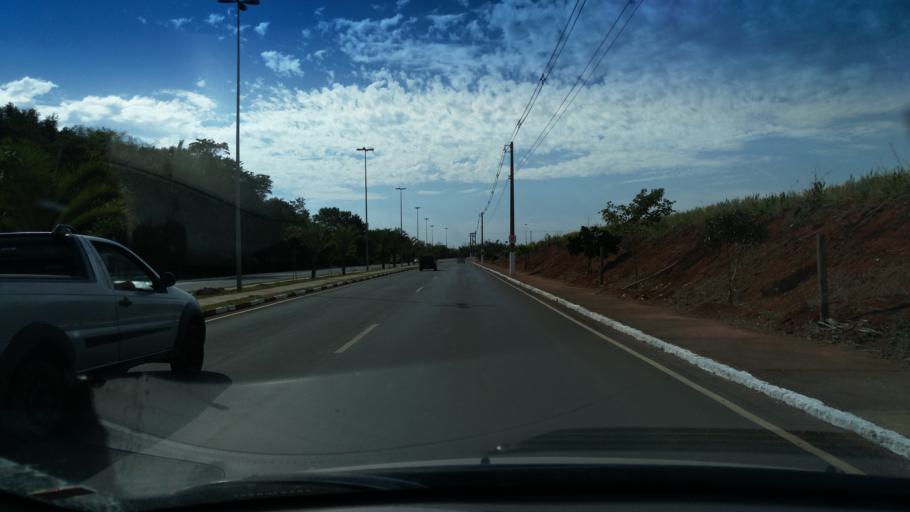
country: BR
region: Sao Paulo
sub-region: Jaguariuna
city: Jaguariuna
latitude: -22.6259
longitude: -47.0625
